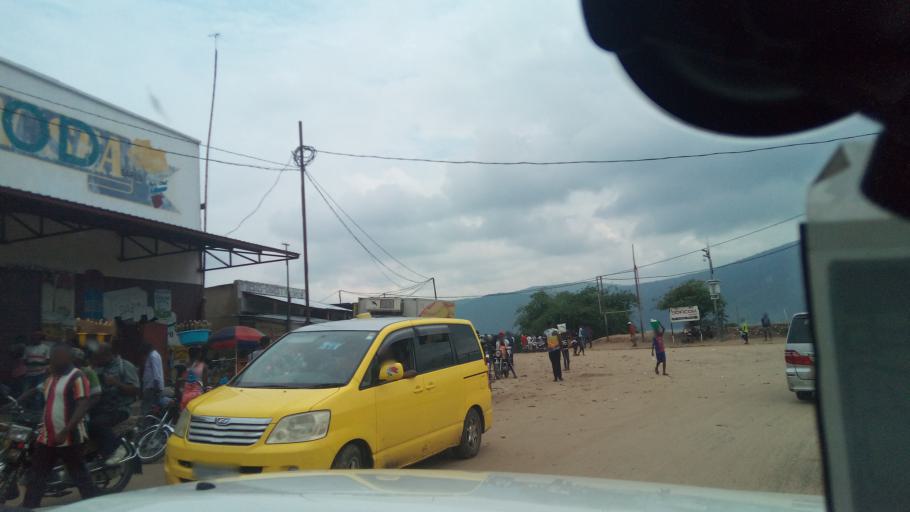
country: CG
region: Brazzaville
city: Brazzaville
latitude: -4.0596
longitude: 15.5529
